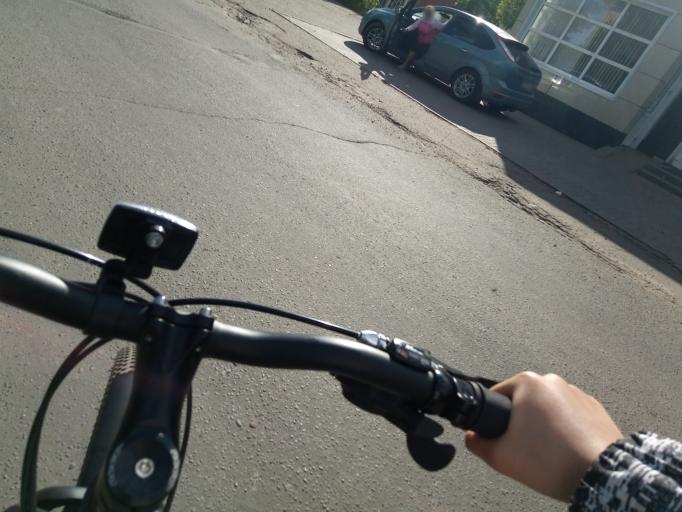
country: RU
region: Jaroslavl
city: Yaroslavl
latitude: 57.6434
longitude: 39.9172
